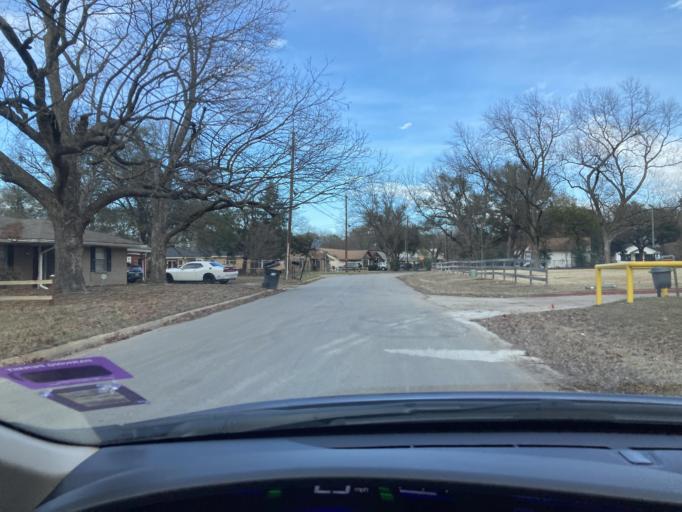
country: US
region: Texas
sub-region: Navarro County
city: Corsicana
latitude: 32.0799
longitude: -96.4907
